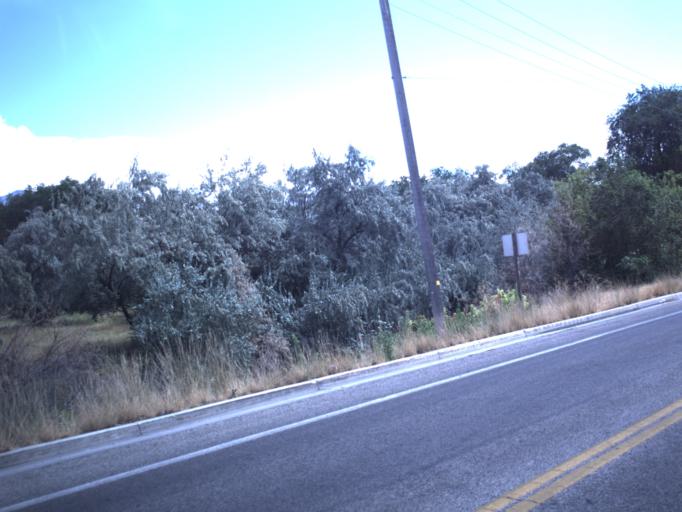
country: US
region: Utah
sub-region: Box Elder County
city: Tremonton
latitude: 41.7134
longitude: -112.1618
